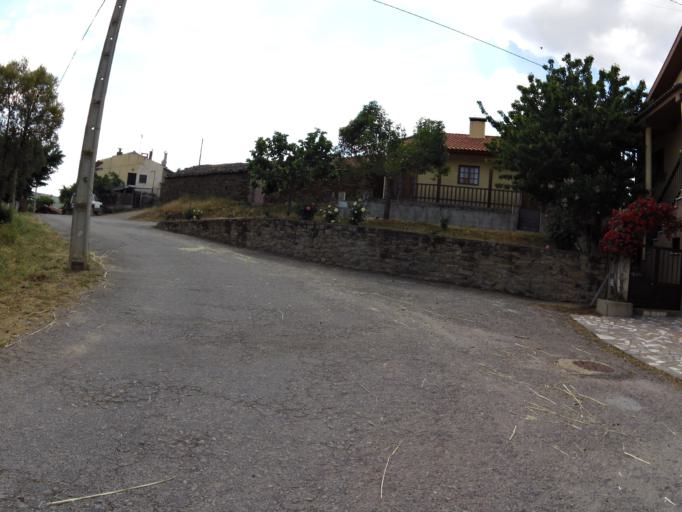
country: PT
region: Braganca
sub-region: Mogadouro
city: Mogadouro
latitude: 41.2456
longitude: -6.7736
